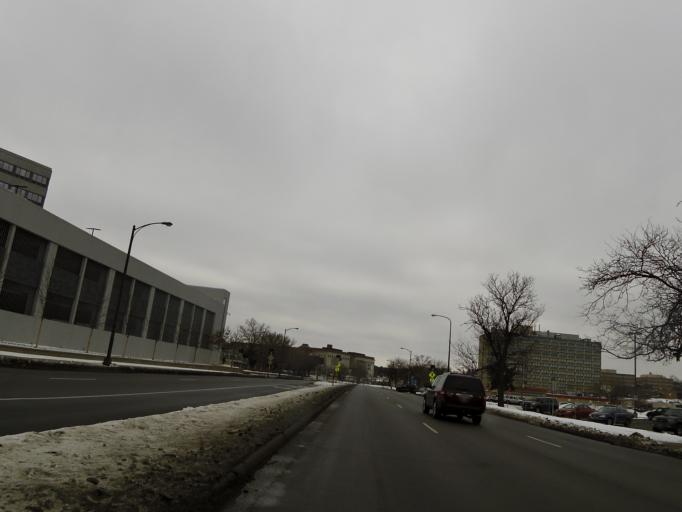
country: US
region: Minnesota
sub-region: Ramsey County
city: Saint Paul
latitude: 44.9539
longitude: -93.1060
